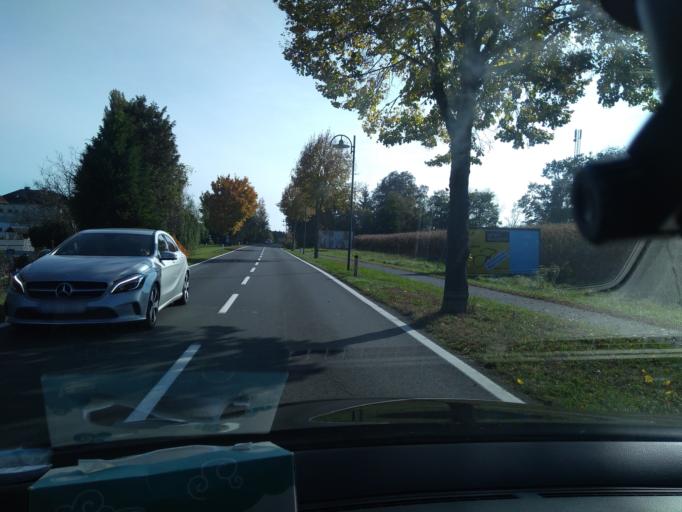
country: AT
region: Styria
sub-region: Politischer Bezirk Leibnitz
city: Kaindorf an der Sulm
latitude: 46.8241
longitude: 15.5446
